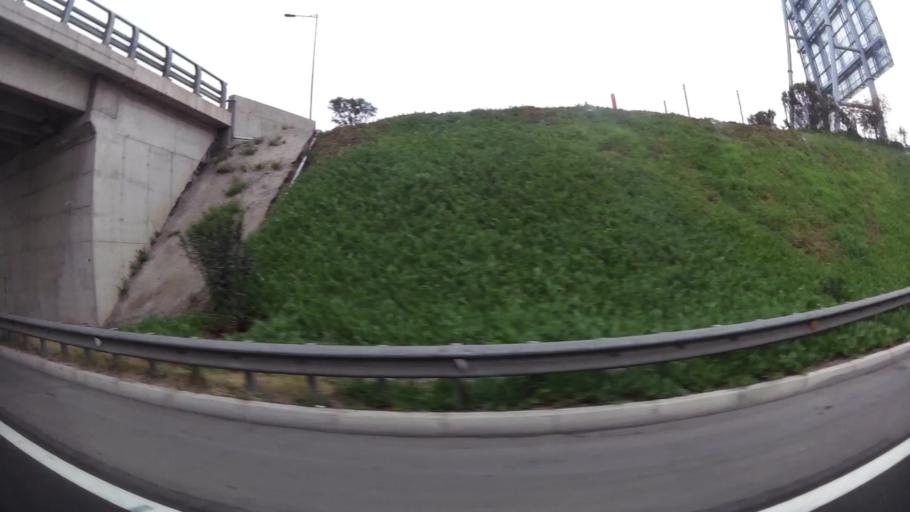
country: CL
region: Santiago Metropolitan
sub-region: Provincia de Santiago
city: Lo Prado
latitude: -33.4160
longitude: -70.7835
